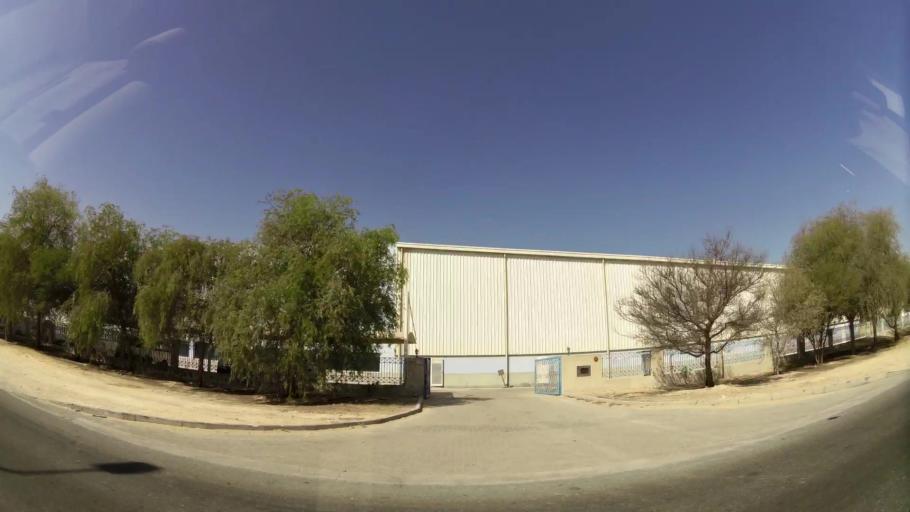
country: AE
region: Dubai
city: Dubai
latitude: 24.9400
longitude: 55.0661
